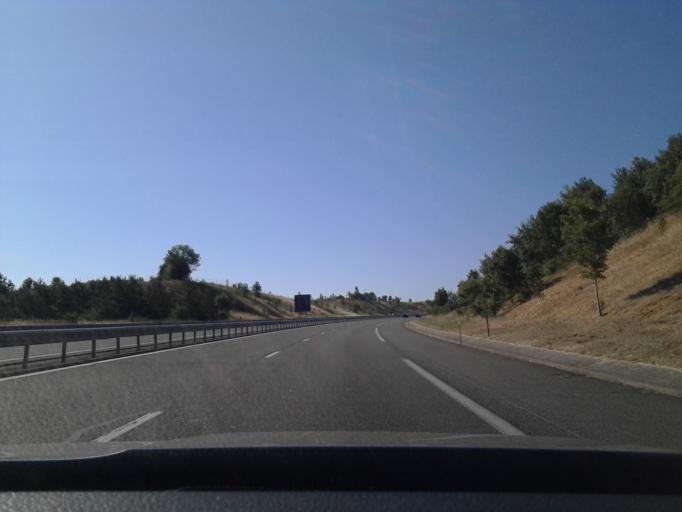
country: FR
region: Midi-Pyrenees
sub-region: Departement de l'Aveyron
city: Severac-le-Chateau
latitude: 44.3124
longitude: 3.1015
